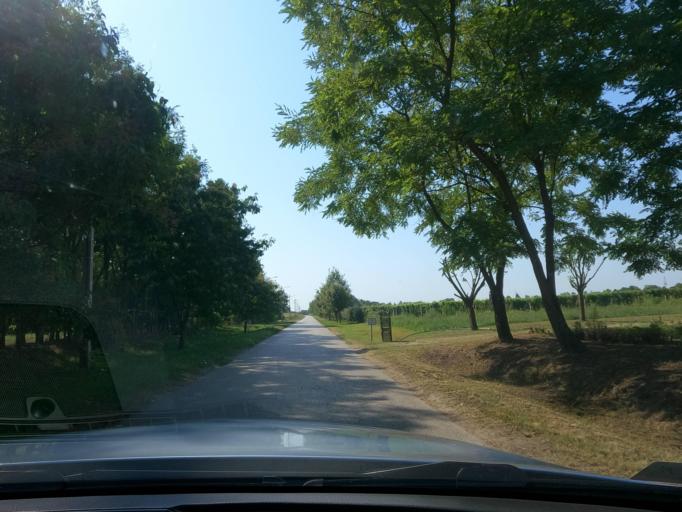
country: HU
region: Csongrad
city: Asotthalom
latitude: 46.0930
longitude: 19.7811
